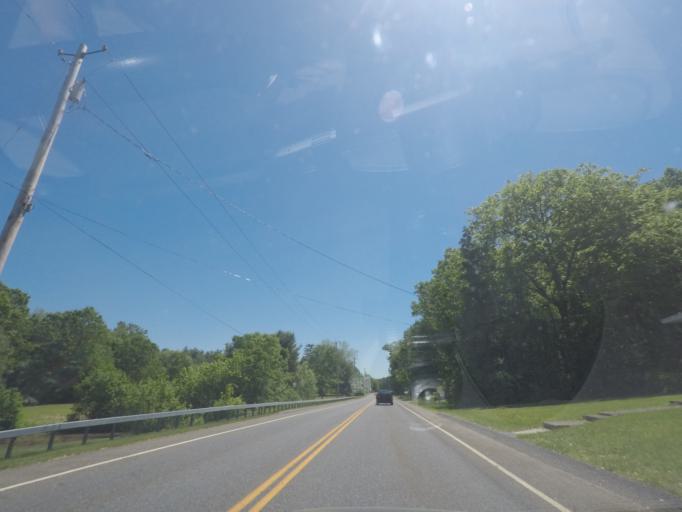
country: US
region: New York
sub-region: Saratoga County
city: Mechanicville
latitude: 42.9464
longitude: -73.7148
